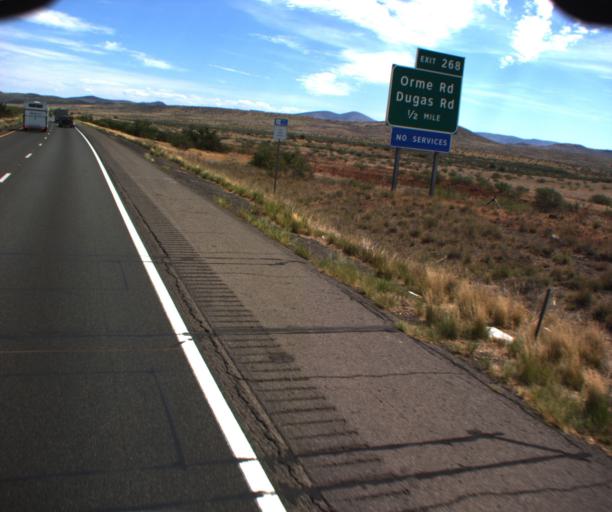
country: US
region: Arizona
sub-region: Yavapai County
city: Cordes Lakes
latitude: 34.3915
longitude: -112.0828
